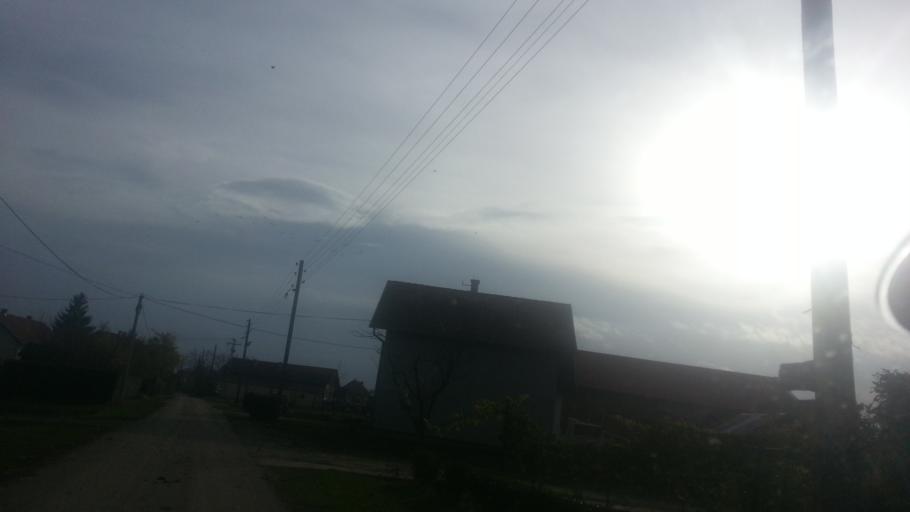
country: RS
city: Putinci
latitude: 44.9967
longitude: 19.9632
